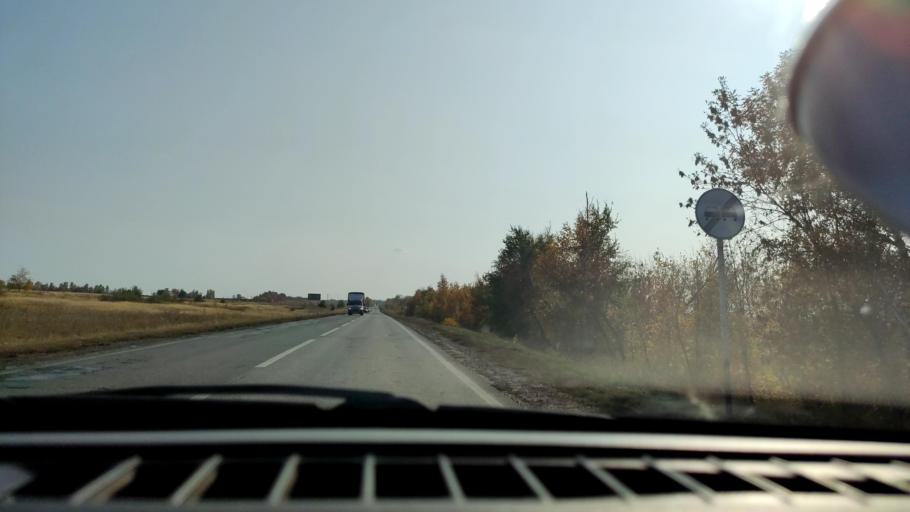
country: RU
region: Samara
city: Smyshlyayevka
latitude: 53.1033
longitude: 50.3500
